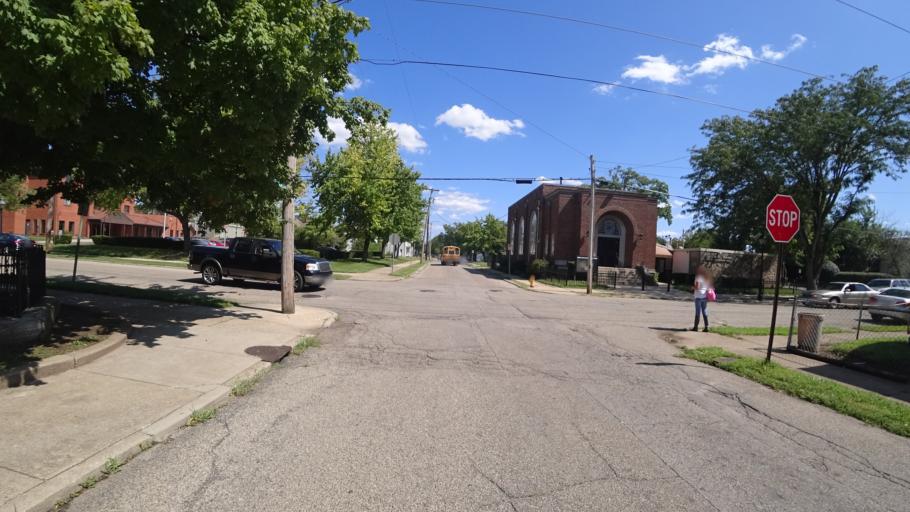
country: US
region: Ohio
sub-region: Butler County
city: Hamilton
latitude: 39.3993
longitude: -84.5555
